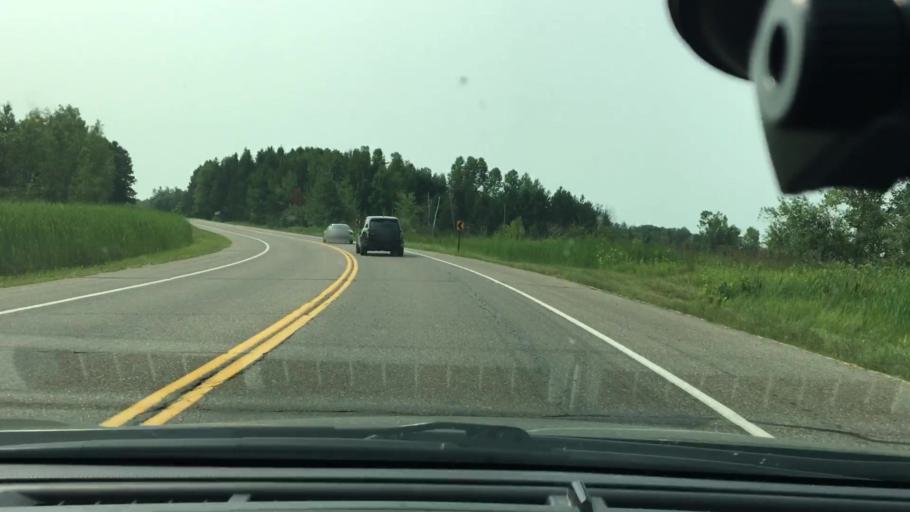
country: US
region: Minnesota
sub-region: Crow Wing County
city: Brainerd
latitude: 46.3970
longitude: -94.2233
